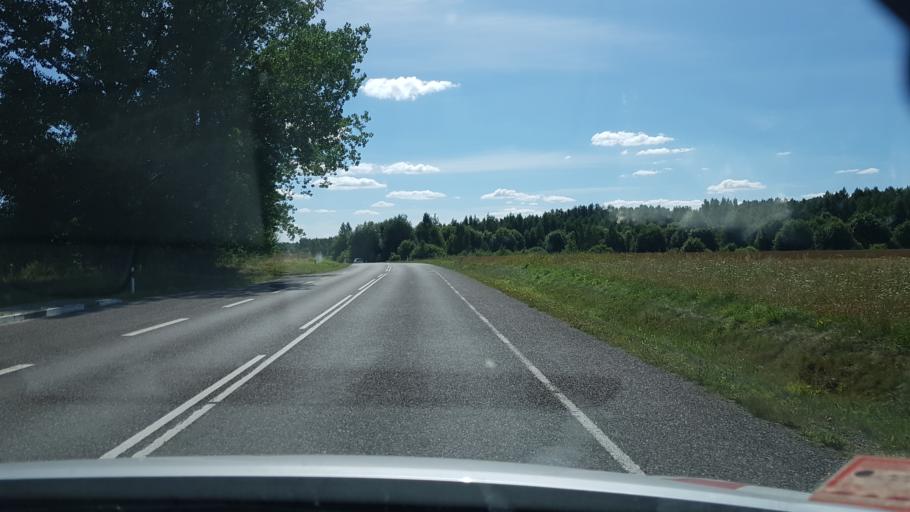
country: EE
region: Polvamaa
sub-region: Raepina vald
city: Rapina
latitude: 58.0707
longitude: 27.5436
